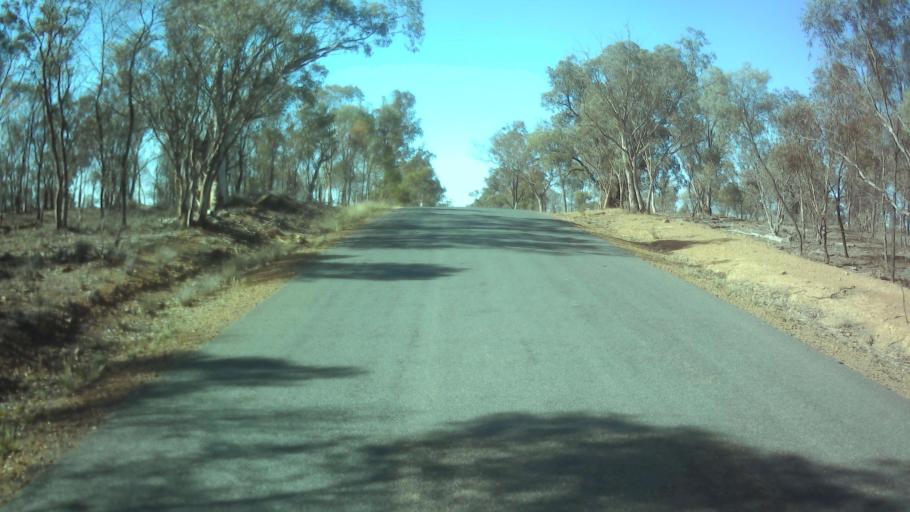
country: AU
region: New South Wales
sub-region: Forbes
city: Forbes
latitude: -33.7053
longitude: 147.8057
